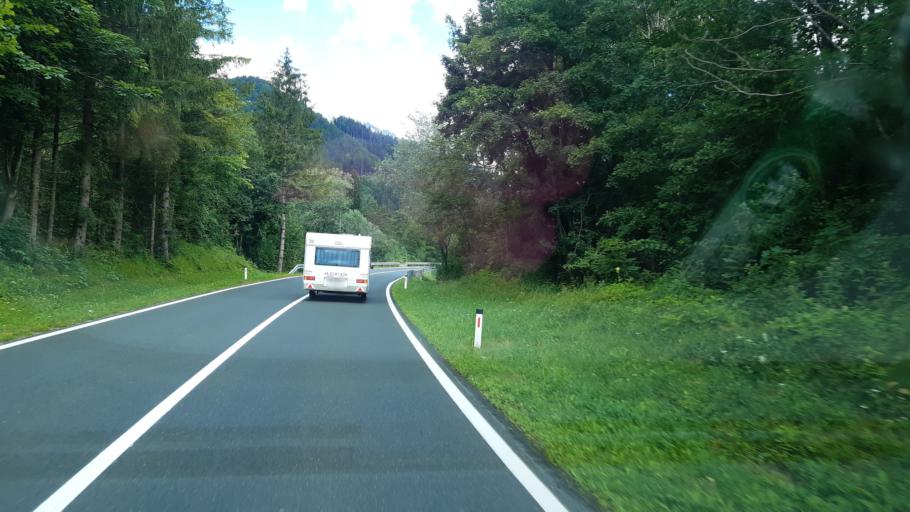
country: SI
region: Trzic
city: Trzic
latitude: 46.3856
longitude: 14.2920
